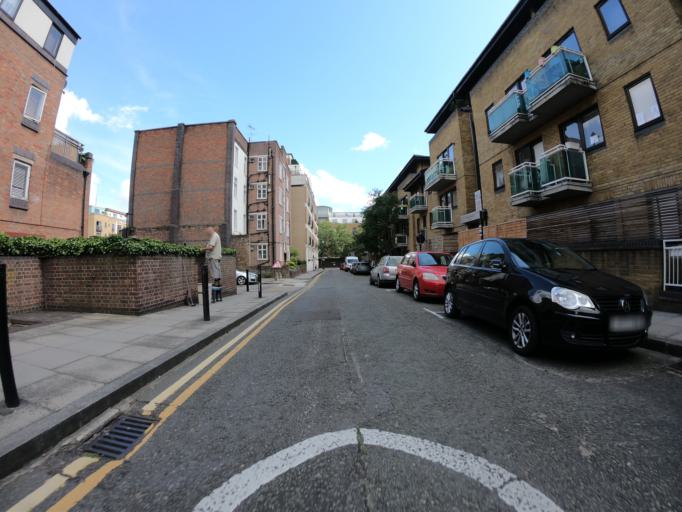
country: GB
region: England
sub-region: Greater London
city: Bethnal Green
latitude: 51.5092
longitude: -0.0706
